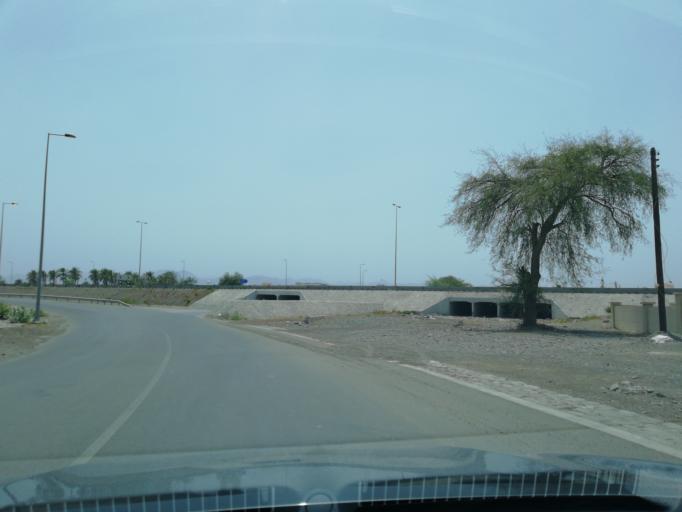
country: OM
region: Al Batinah
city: Shinas
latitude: 24.7370
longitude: 56.4571
